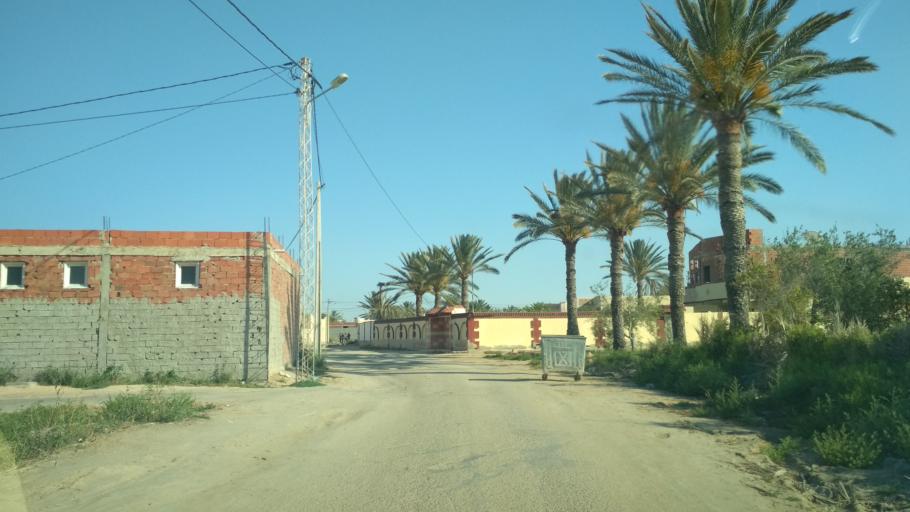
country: TN
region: Qabis
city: Gabes
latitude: 33.9478
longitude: 10.0636
